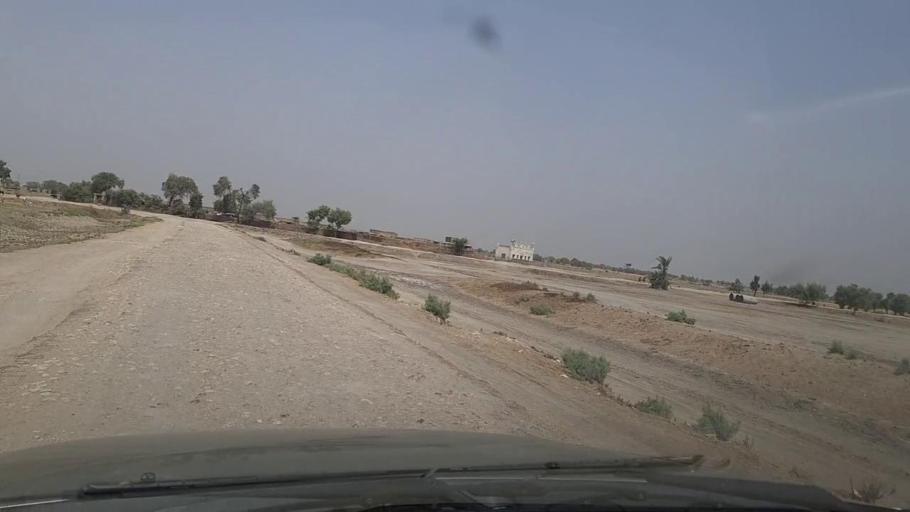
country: PK
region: Balochistan
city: Sohbatpur
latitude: 28.4153
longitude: 68.6892
